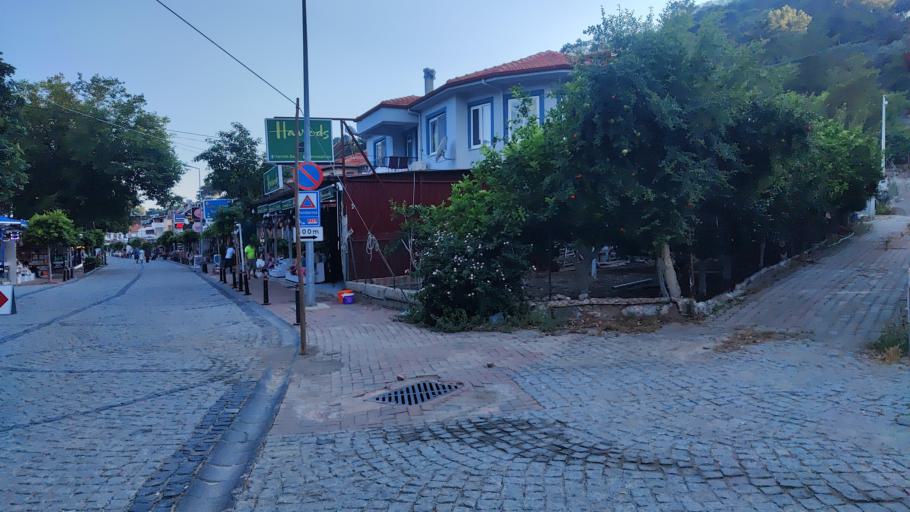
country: TR
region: Mugla
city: Sarigerme
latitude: 36.7141
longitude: 28.7037
